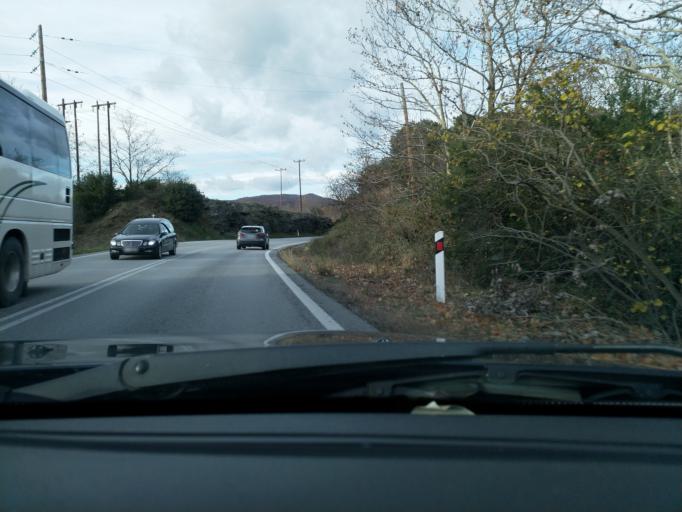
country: GR
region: Thessaly
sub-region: Trikala
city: Kastraki
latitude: 39.7191
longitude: 21.5953
